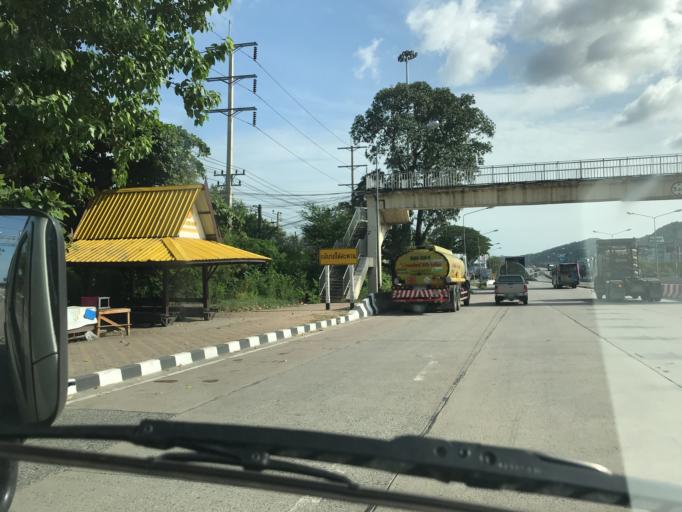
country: TH
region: Chon Buri
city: Bang Lamung
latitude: 13.1066
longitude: 100.9158
